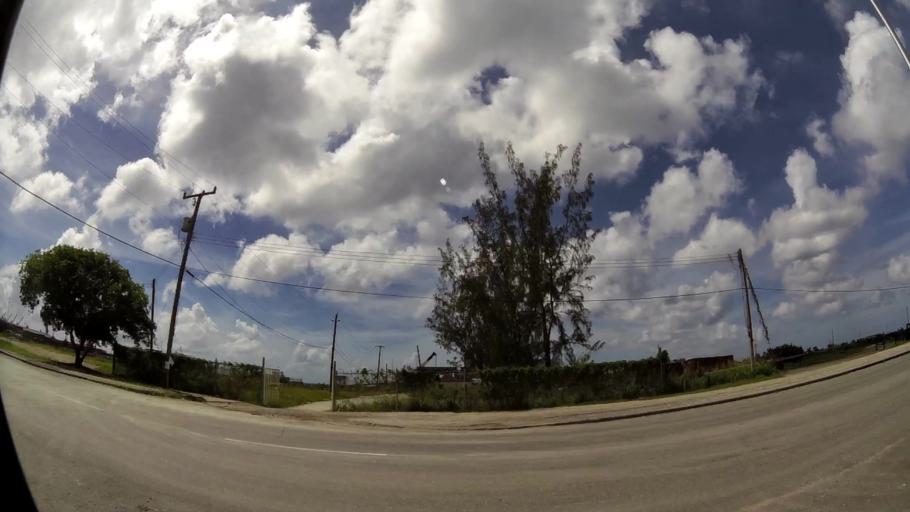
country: BB
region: Saint Michael
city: Bridgetown
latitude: 13.1111
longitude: -59.6268
